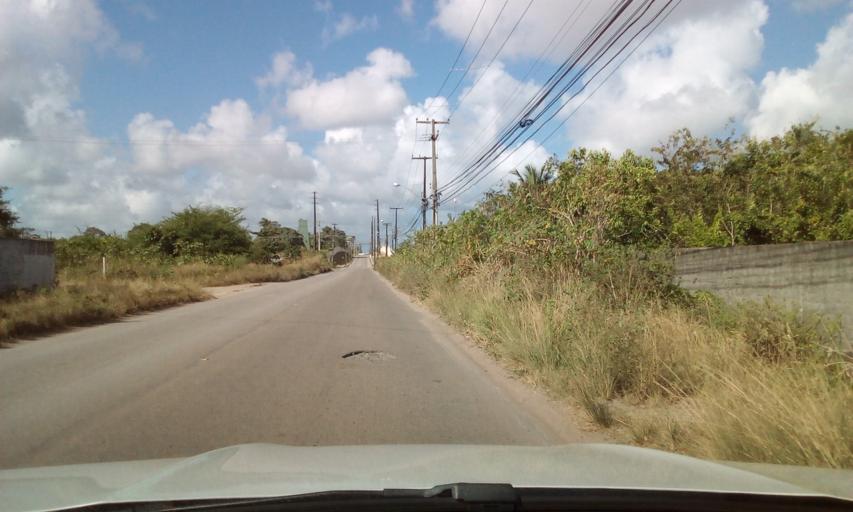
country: BR
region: Paraiba
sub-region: Bayeux
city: Bayeux
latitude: -7.1822
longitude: -34.9098
